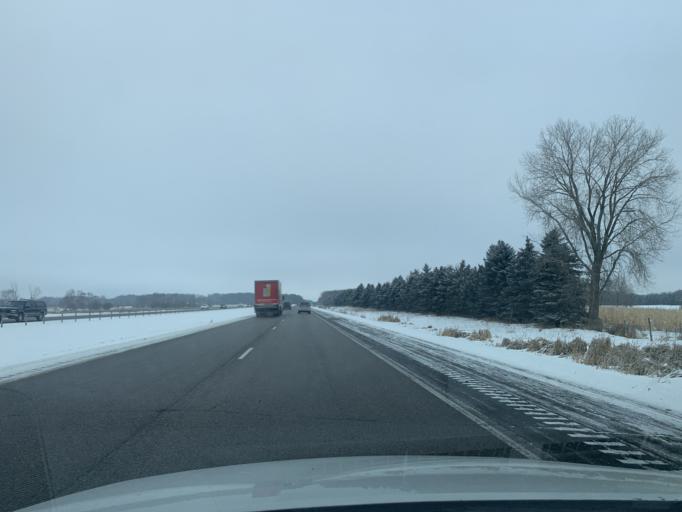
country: US
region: Minnesota
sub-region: Chisago County
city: Stacy
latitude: 45.4274
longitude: -92.9898
